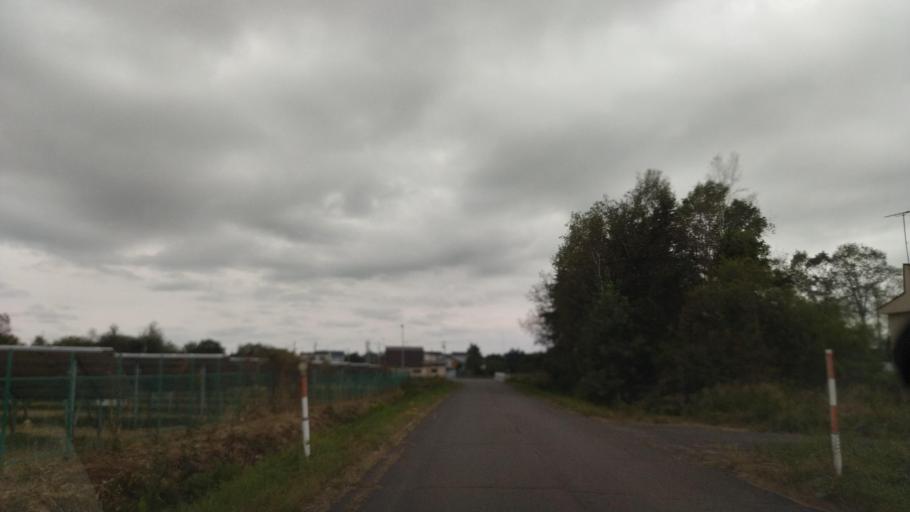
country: JP
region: Hokkaido
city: Otofuke
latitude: 43.2410
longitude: 143.2951
